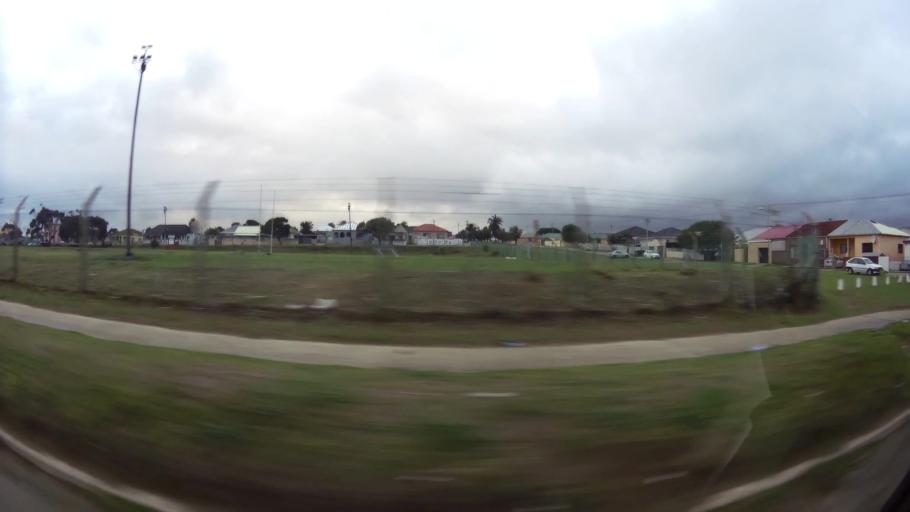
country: ZA
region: Eastern Cape
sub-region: Nelson Mandela Bay Metropolitan Municipality
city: Port Elizabeth
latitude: -33.9284
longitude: 25.5954
